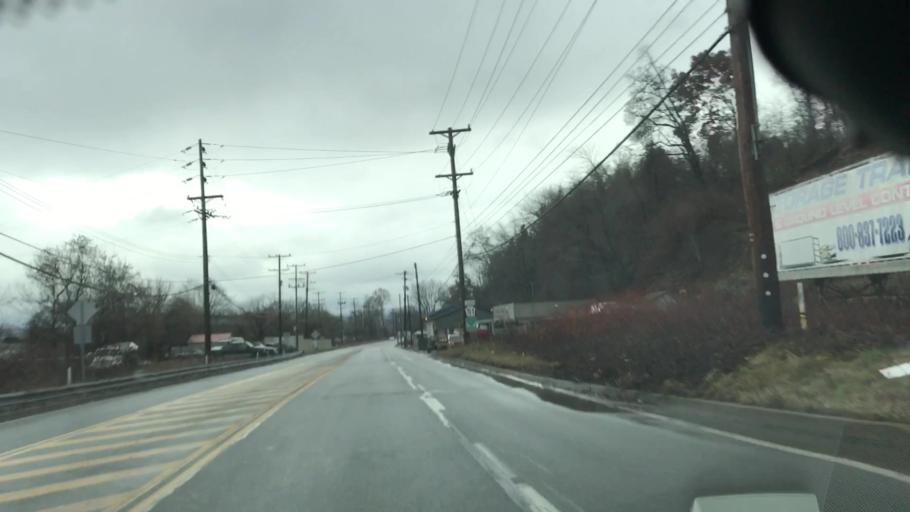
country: US
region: Pennsylvania
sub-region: Beaver County
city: Monaca
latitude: 40.6815
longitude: -80.2649
